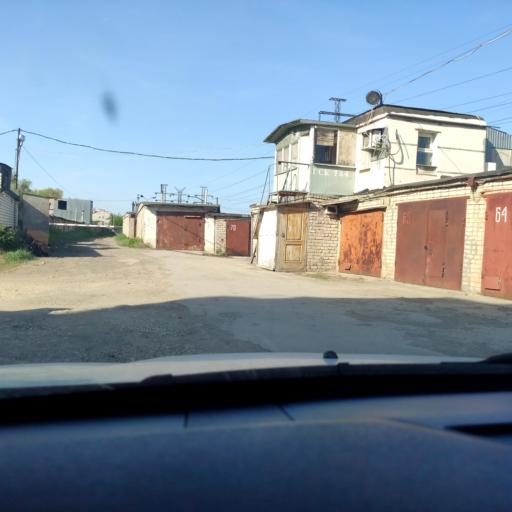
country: RU
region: Samara
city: Smyshlyayevka
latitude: 53.2190
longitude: 50.2796
